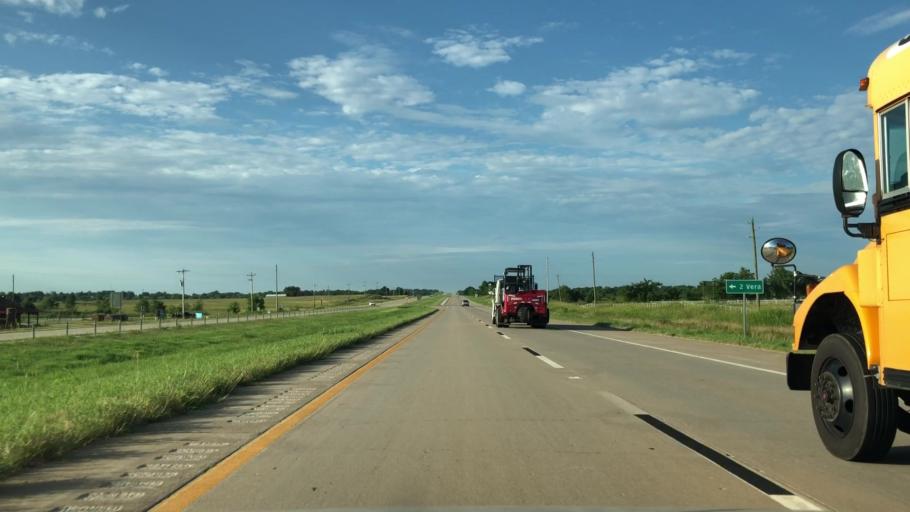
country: US
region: Oklahoma
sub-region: Osage County
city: Skiatook
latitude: 36.4548
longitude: -95.9207
